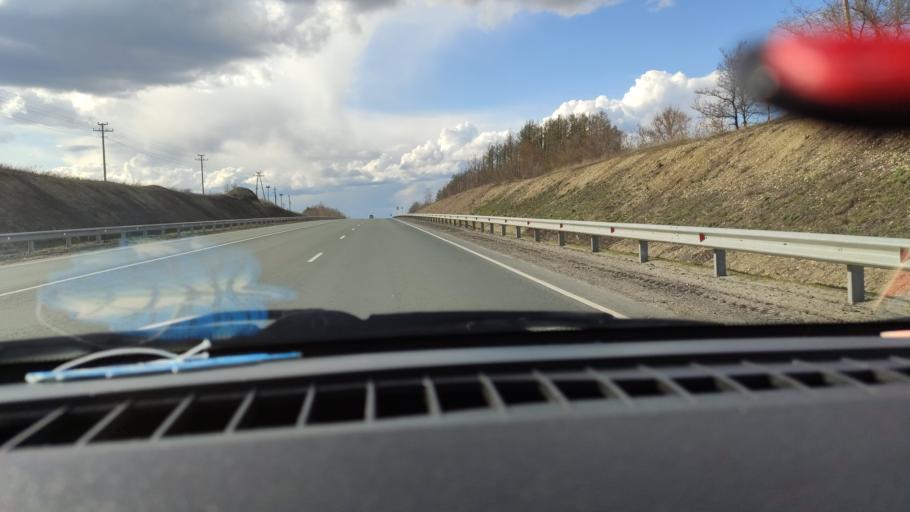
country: RU
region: Saratov
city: Shikhany
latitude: 52.1463
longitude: 47.1973
